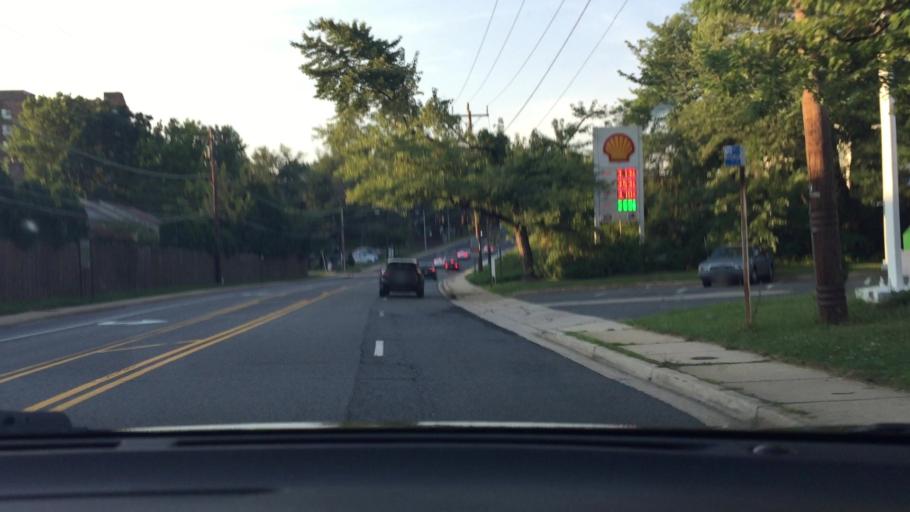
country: US
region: Maryland
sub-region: Montgomery County
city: North Bethesda
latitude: 39.0232
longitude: -77.1499
